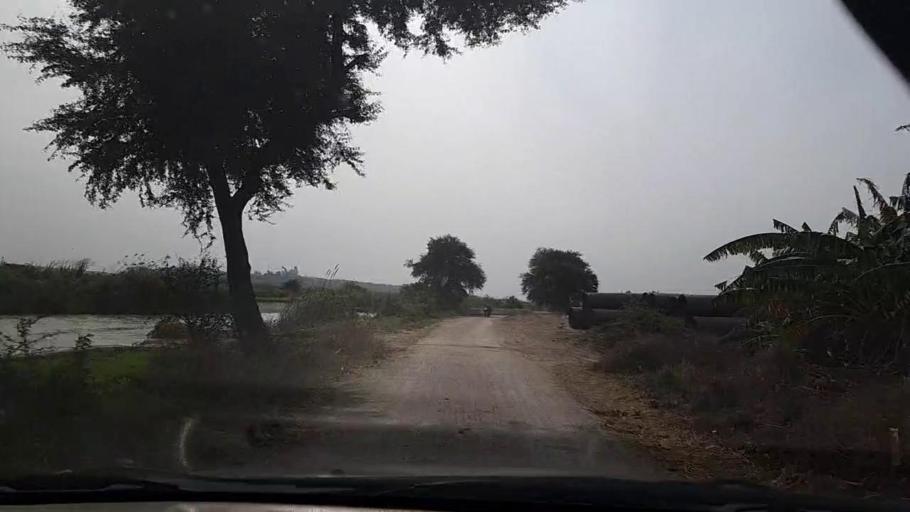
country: PK
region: Sindh
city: Thatta
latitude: 24.5741
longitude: 67.8787
